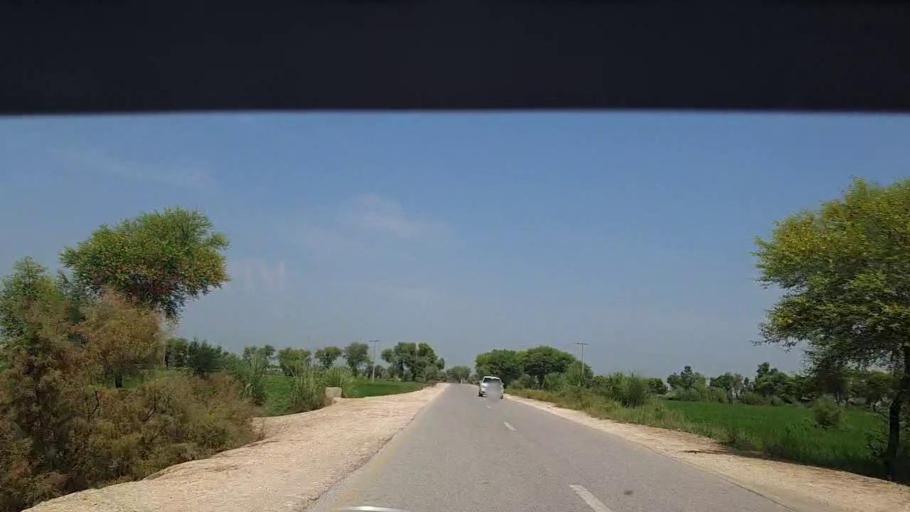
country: PK
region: Sindh
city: Thul
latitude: 28.1410
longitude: 68.8176
